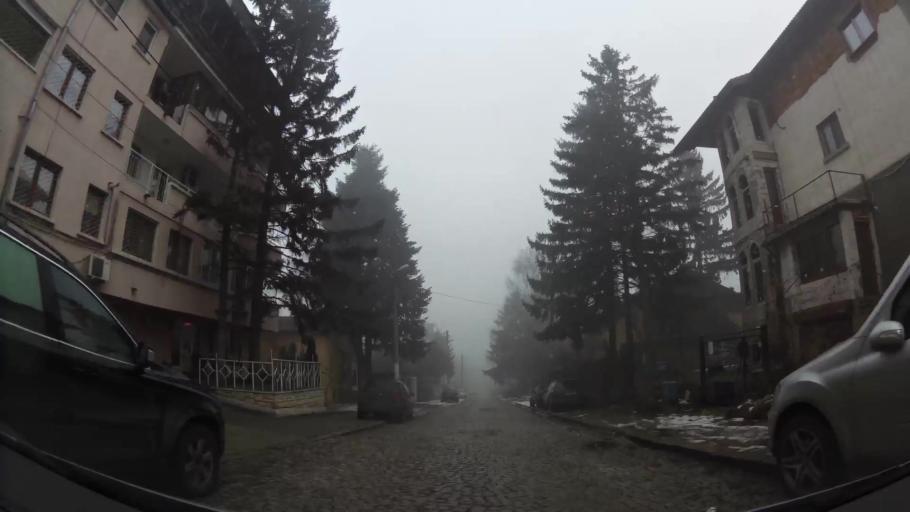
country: BG
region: Sofia-Capital
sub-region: Stolichna Obshtina
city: Sofia
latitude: 42.6627
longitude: 23.2596
